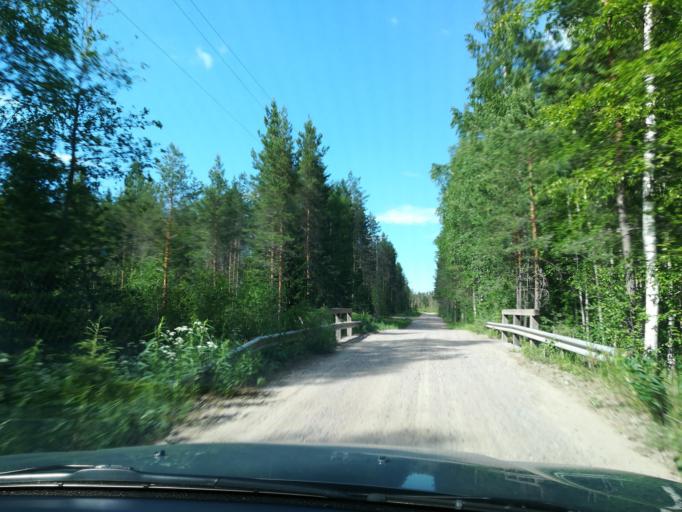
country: FI
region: South Karelia
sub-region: Imatra
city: Ruokolahti
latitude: 61.5345
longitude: 28.8349
